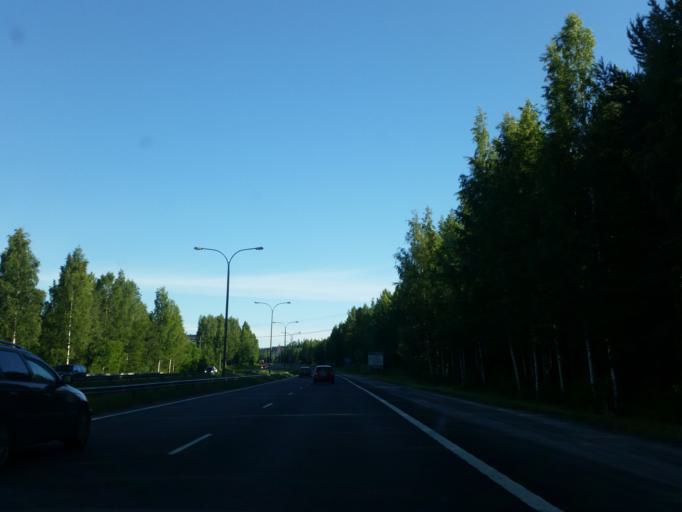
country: FI
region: Northern Savo
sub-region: Kuopio
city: Kuopio
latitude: 62.8729
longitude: 27.6206
